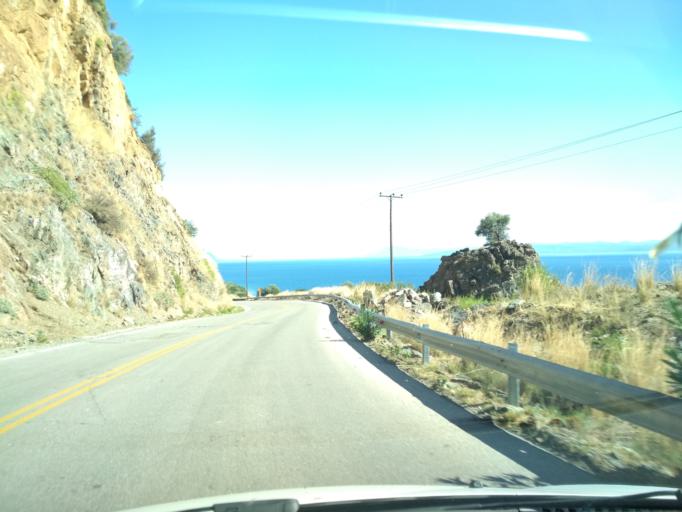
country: GR
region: Central Greece
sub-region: Nomos Evvoias
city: Roviai
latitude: 38.8455
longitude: 23.1641
